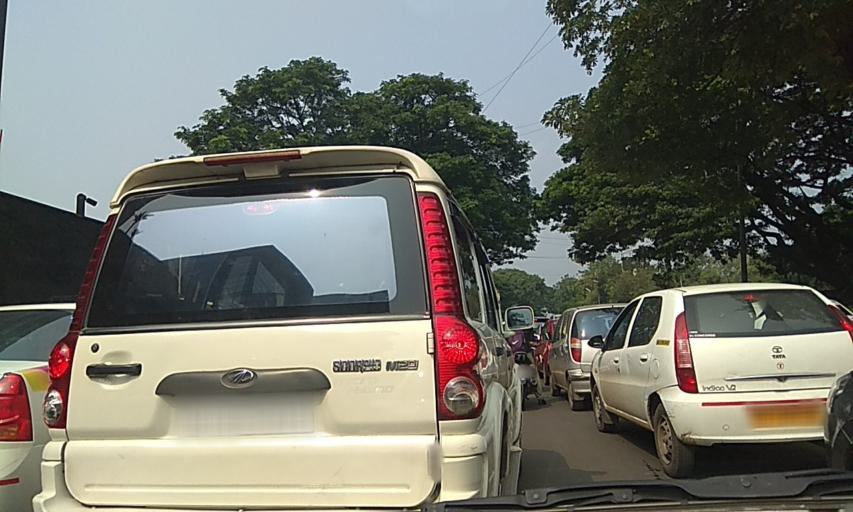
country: IN
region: Maharashtra
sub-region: Pune Division
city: Khadki
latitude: 18.5526
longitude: 73.8903
